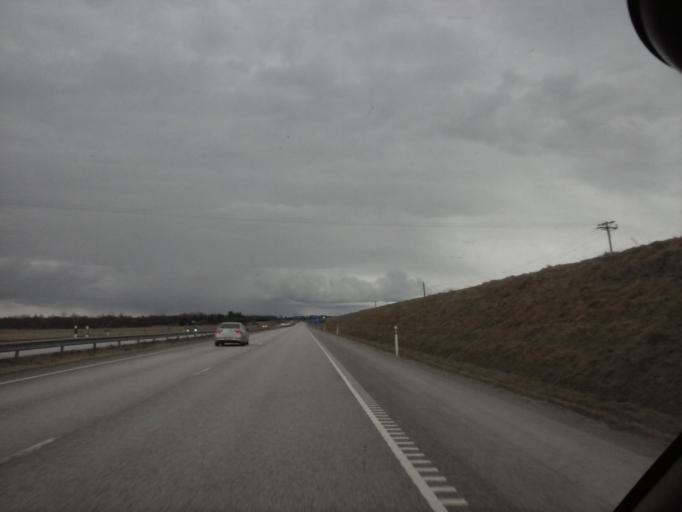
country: EE
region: Jaervamaa
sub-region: Paide linn
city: Paide
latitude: 58.9284
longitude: 25.6124
